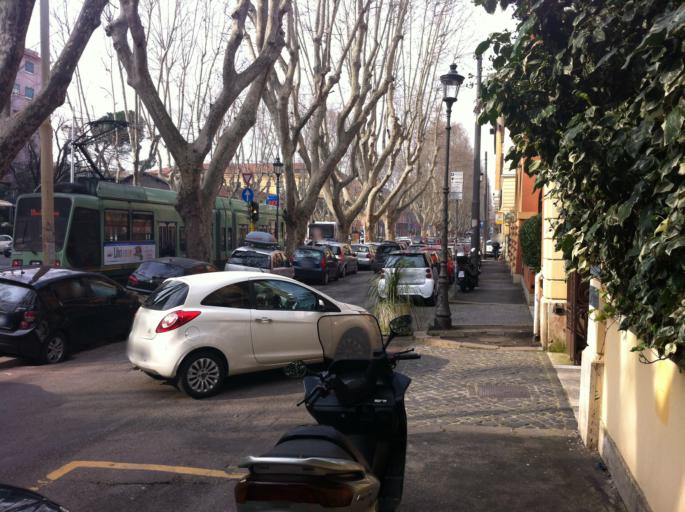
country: VA
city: Vatican City
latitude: 41.9136
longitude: 12.4675
